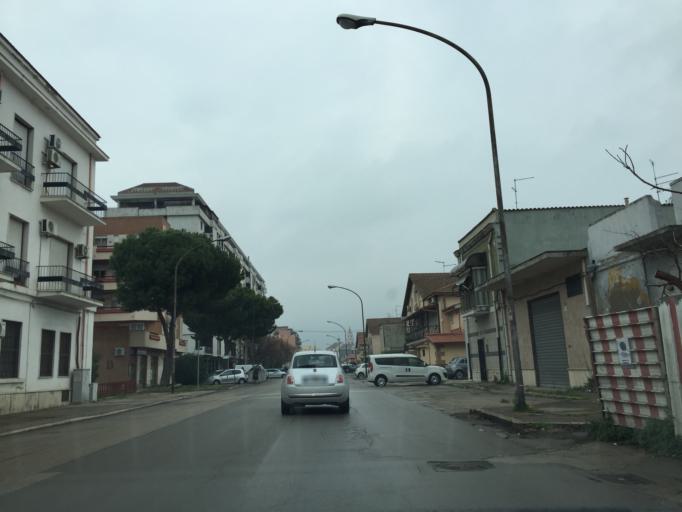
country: IT
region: Apulia
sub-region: Provincia di Foggia
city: Foggia
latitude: 41.4699
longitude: 15.5392
